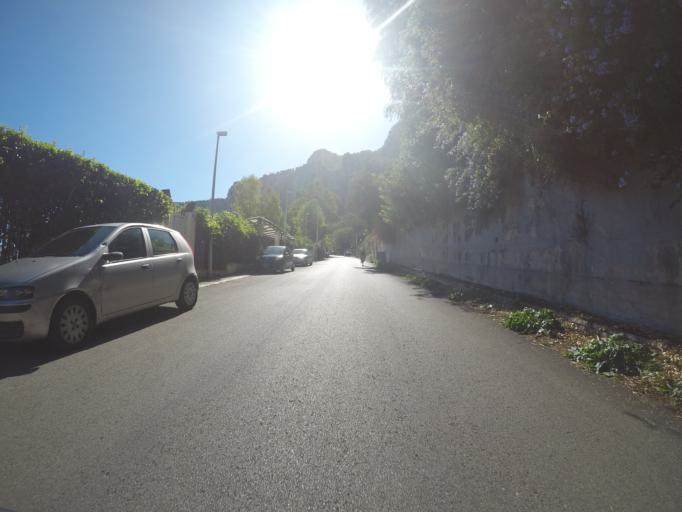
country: IT
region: Sicily
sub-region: Palermo
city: Palermo
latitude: 38.1894
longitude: 13.3403
